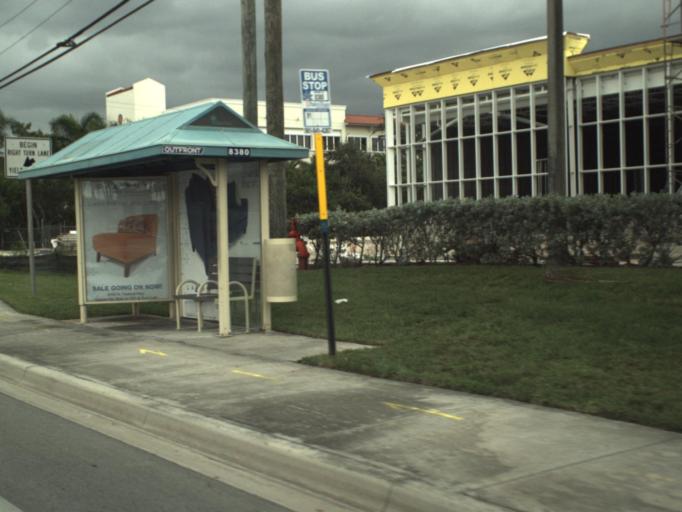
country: US
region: Florida
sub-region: Palm Beach County
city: Boca Pointe
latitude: 26.3681
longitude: -80.1901
